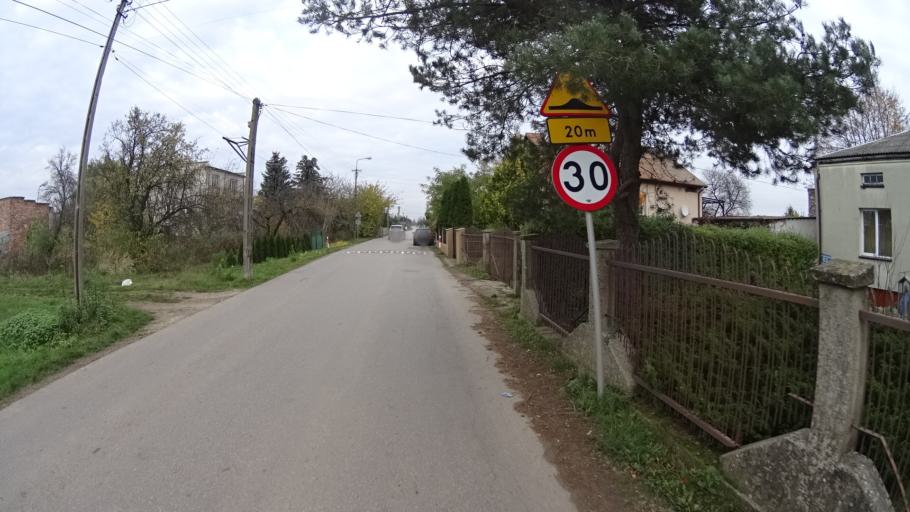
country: PL
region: Masovian Voivodeship
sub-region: Powiat warszawski zachodni
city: Stare Babice
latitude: 52.2397
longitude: 20.8291
